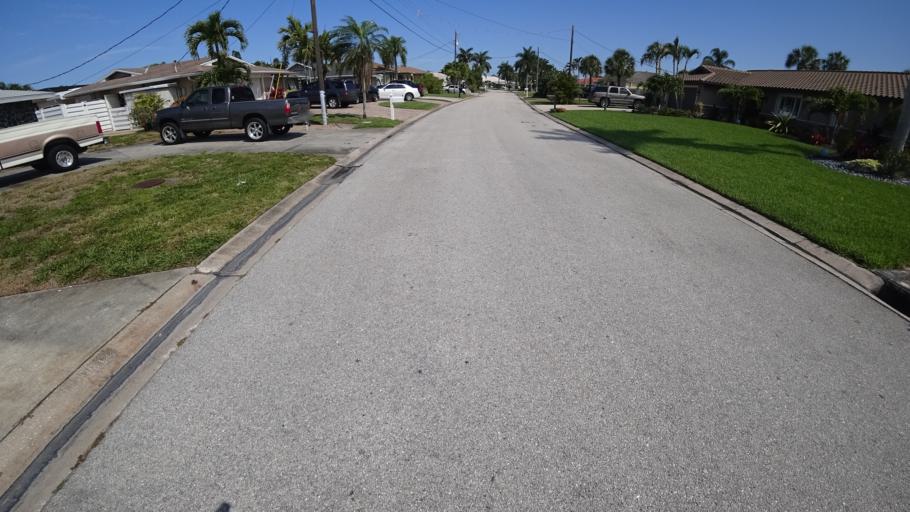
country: US
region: Florida
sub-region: Manatee County
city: Cortez
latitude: 27.4544
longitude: -82.6549
